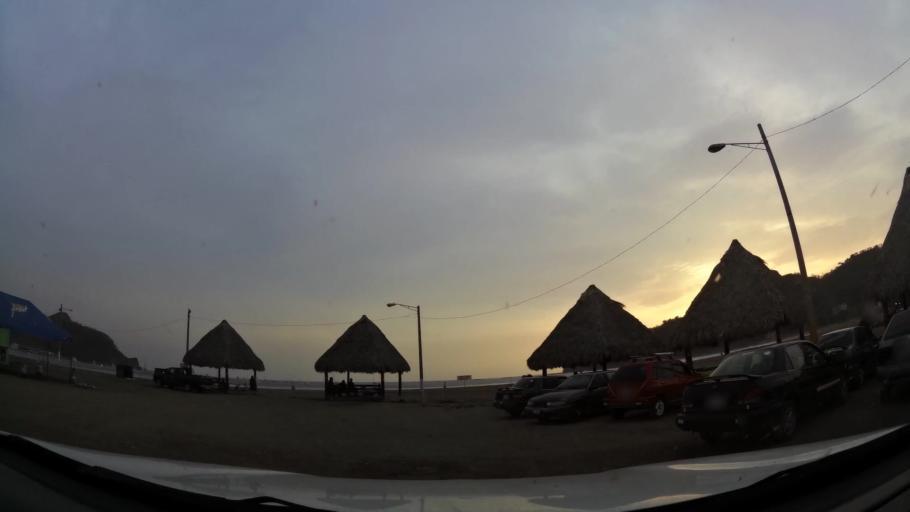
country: NI
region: Rivas
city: San Juan del Sur
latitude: 11.2591
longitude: -85.8740
